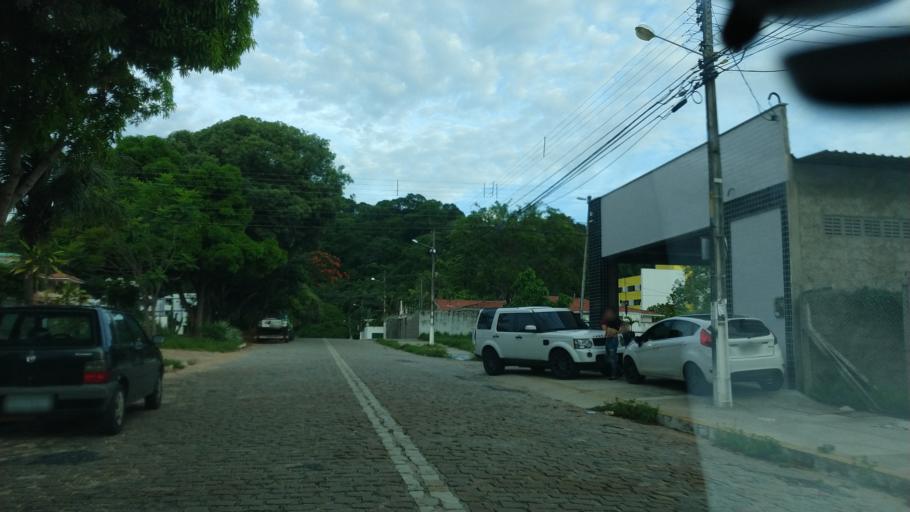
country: BR
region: Rio Grande do Norte
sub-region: Natal
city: Natal
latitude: -5.8182
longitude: -35.1988
